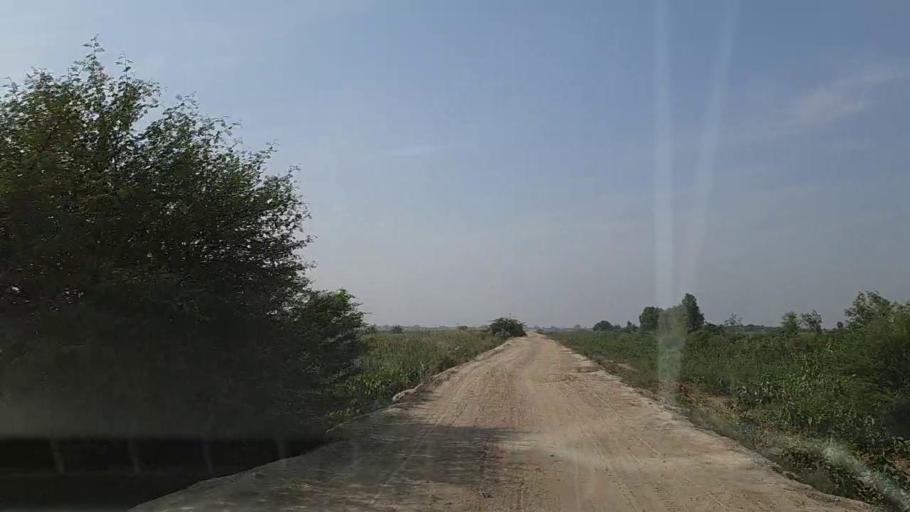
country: PK
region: Sindh
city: Mirpur Batoro
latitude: 24.6509
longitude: 68.2361
